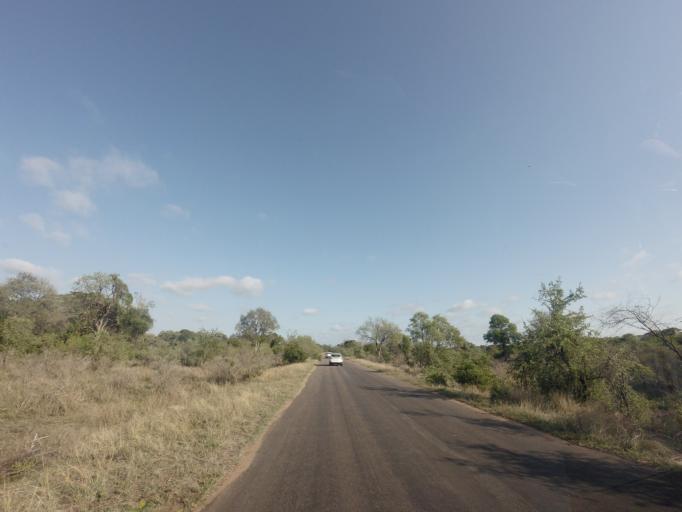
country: ZA
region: Mpumalanga
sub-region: Ehlanzeni District
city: Komatipoort
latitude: -25.2777
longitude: 31.8499
